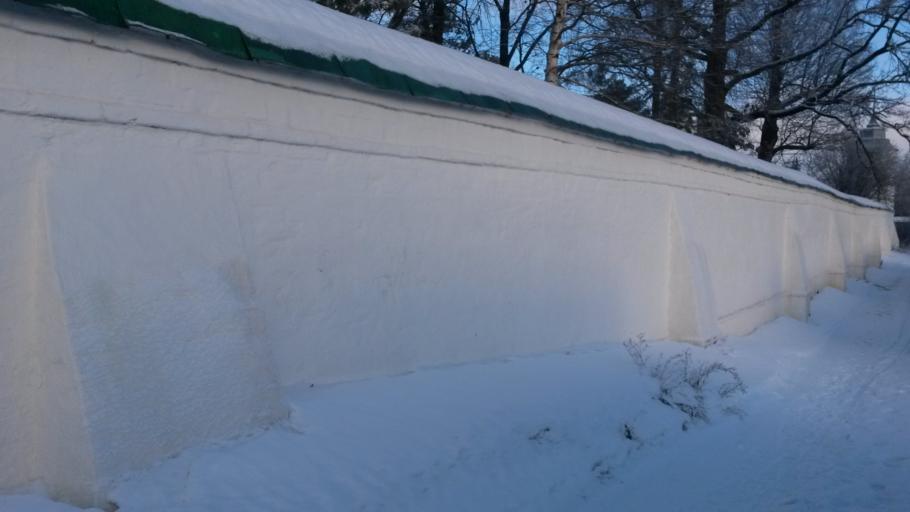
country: RU
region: Jaroslavl
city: Yaroslavl
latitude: 57.6946
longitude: 39.8301
